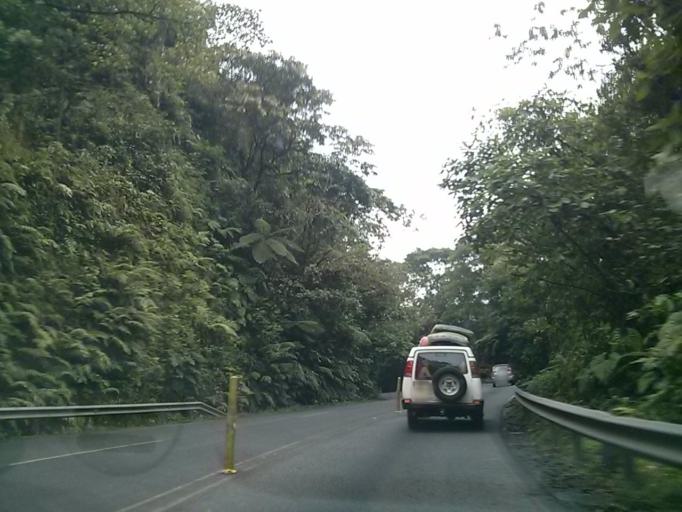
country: CR
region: San Jose
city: Dulce Nombre de Jesus
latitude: 10.1426
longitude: -83.9730
